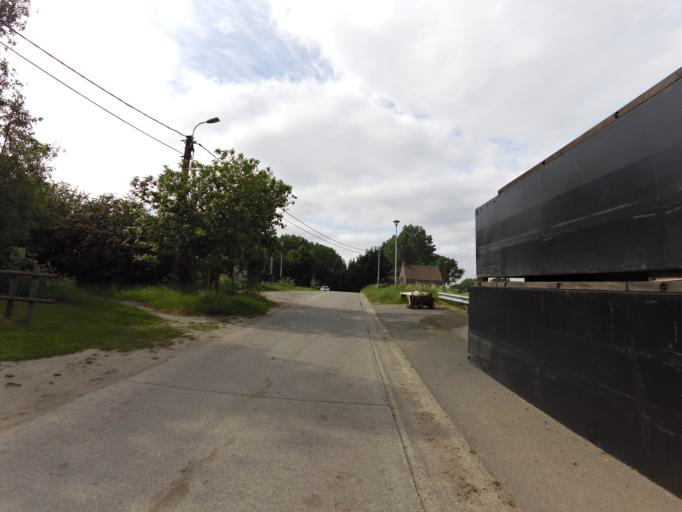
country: BE
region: Flanders
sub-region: Provincie West-Vlaanderen
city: Oostkamp
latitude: 51.1610
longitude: 3.2583
